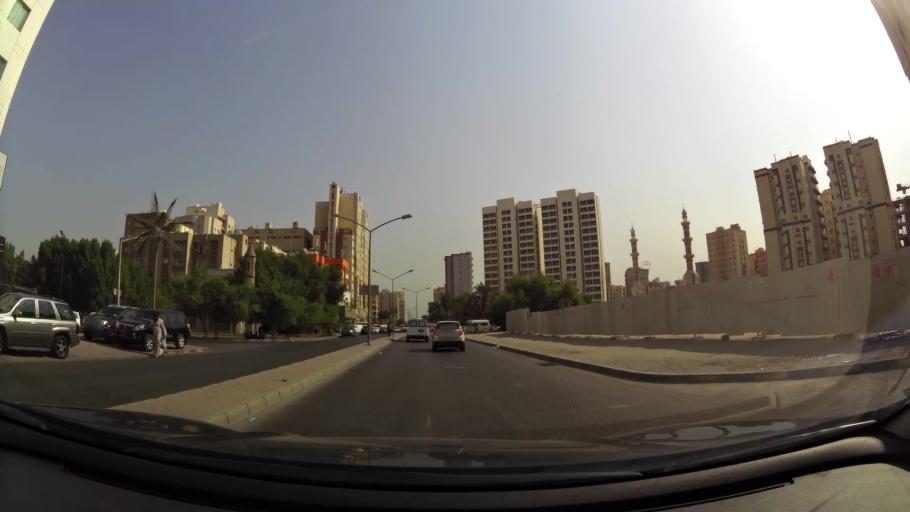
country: KW
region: Muhafazat Hawalli
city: As Salimiyah
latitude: 29.3273
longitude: 48.0565
